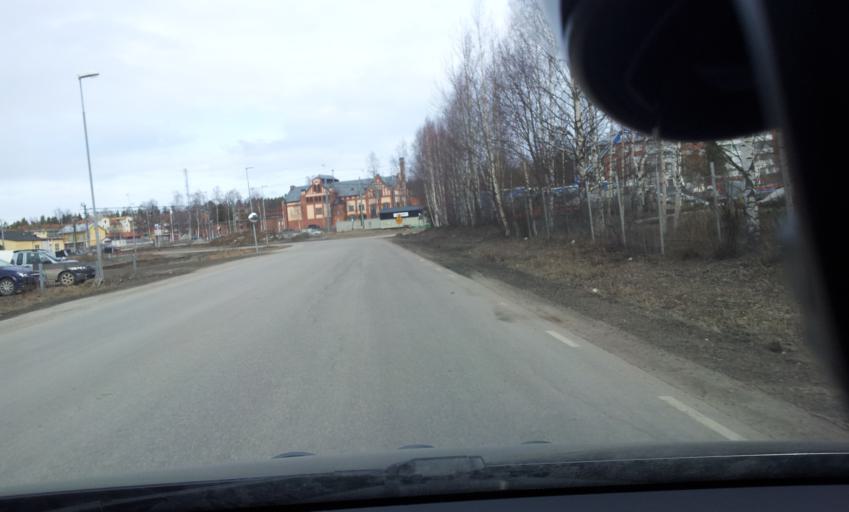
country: SE
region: Gaevleborg
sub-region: Ljusdals Kommun
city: Ljusdal
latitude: 61.8233
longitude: 16.1043
